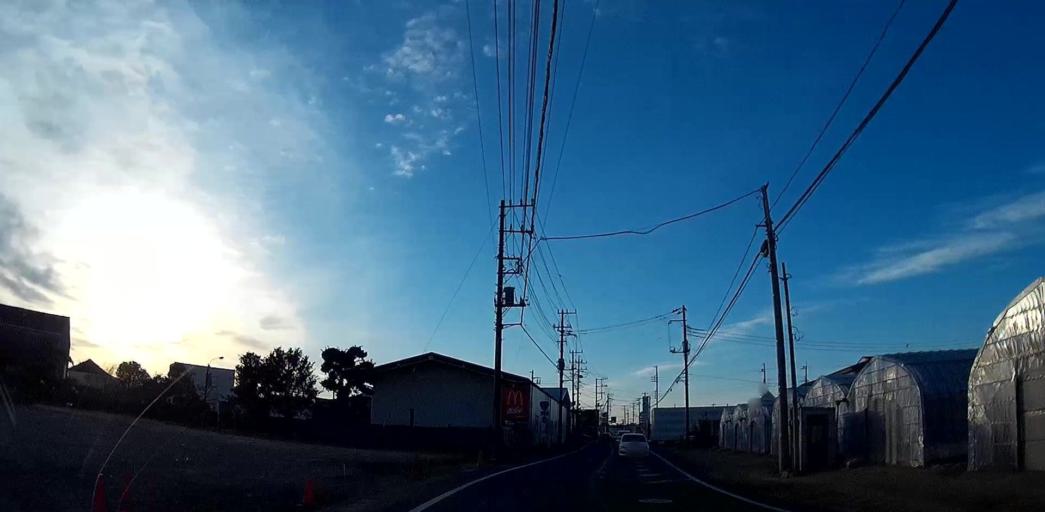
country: JP
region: Chiba
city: Omigawa
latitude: 35.8485
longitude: 140.6169
